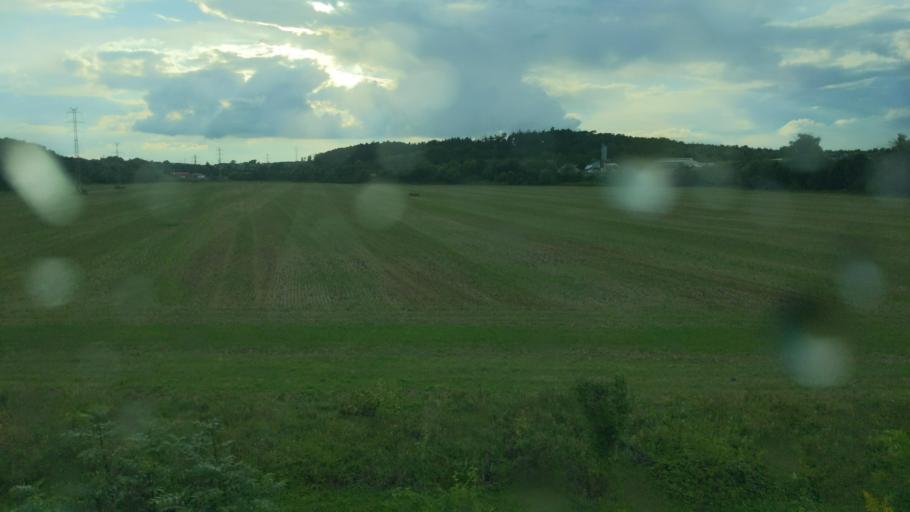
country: CZ
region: Central Bohemia
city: Poricany
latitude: 50.1138
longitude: 14.9418
